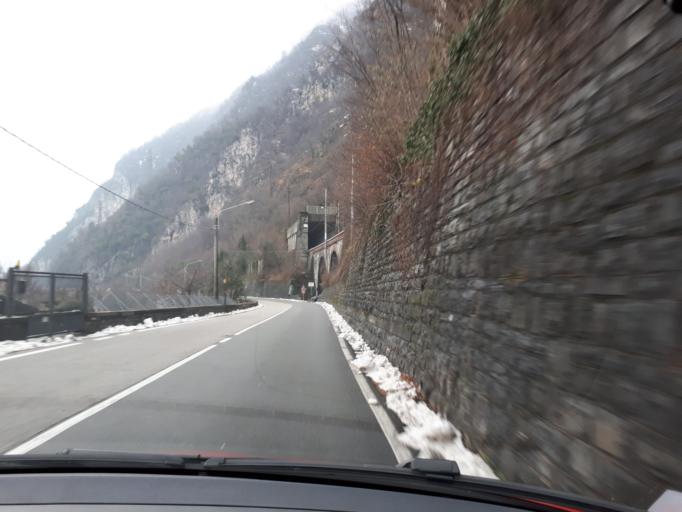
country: IT
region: Lombardy
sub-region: Provincia di Lecco
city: Lierna
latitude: 45.9800
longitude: 9.2973
